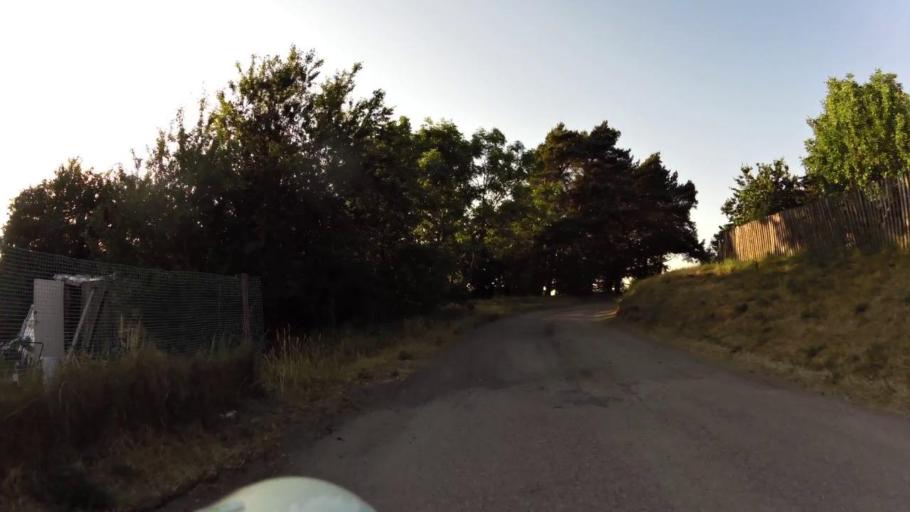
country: PL
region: West Pomeranian Voivodeship
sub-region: Powiat szczecinecki
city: Szczecinek
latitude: 53.8049
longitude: 16.6879
